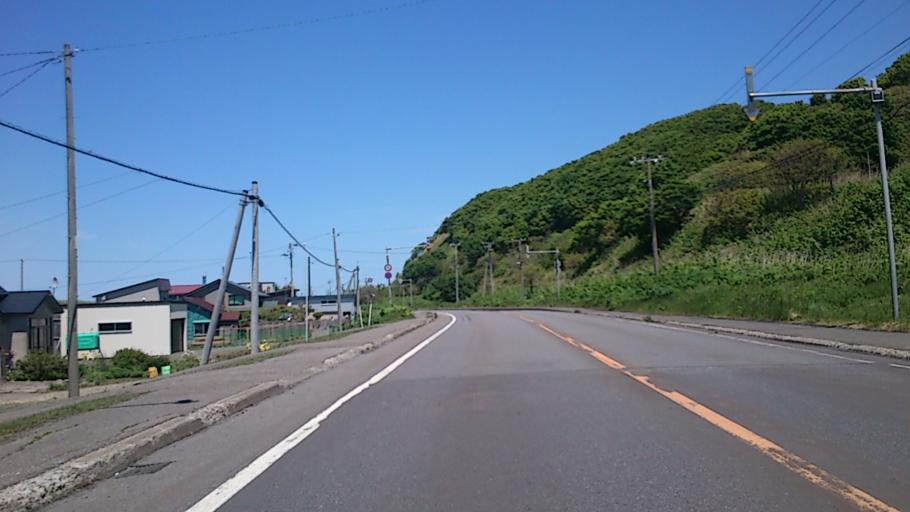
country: JP
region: Hokkaido
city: Rumoi
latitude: 43.9698
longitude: 141.6466
